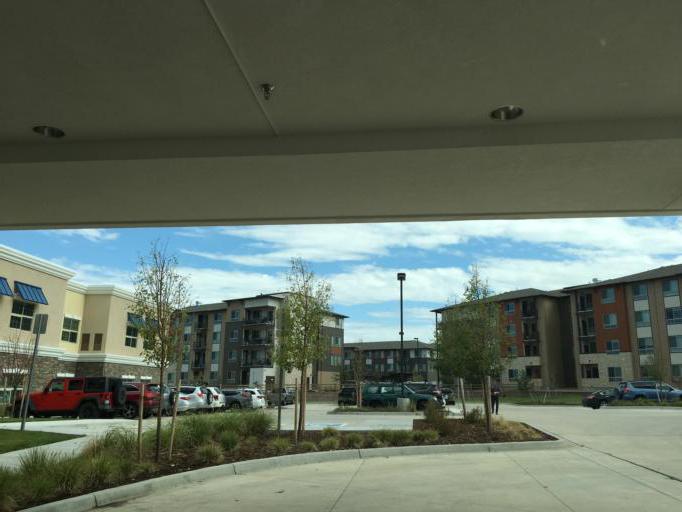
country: US
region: Colorado
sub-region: Jefferson County
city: West Pleasant View
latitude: 39.7271
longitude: -105.2049
